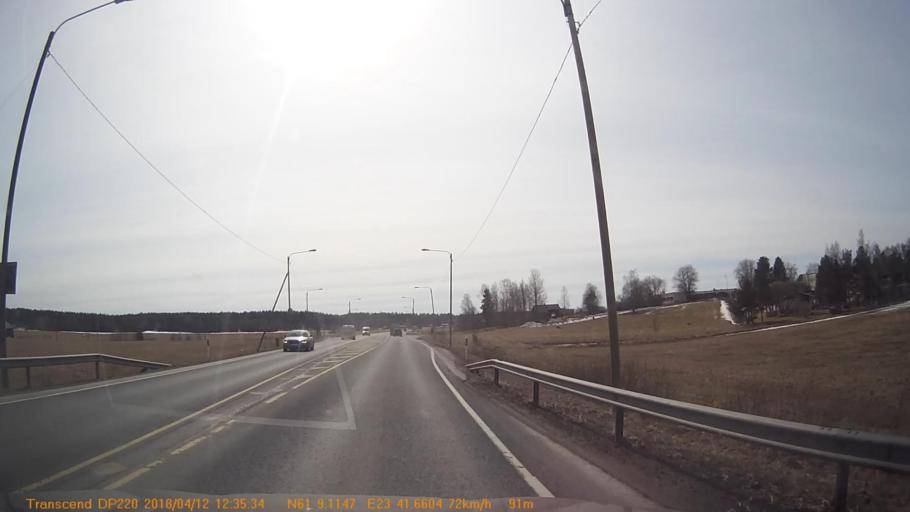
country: FI
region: Pirkanmaa
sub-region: Etelae-Pirkanmaa
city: Kylmaekoski
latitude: 61.1521
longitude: 23.6944
